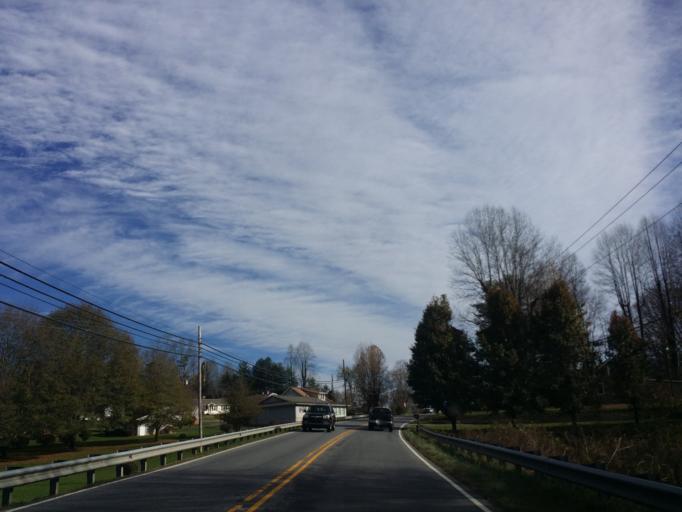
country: US
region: North Carolina
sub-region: McDowell County
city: West Marion
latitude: 35.6875
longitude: -82.0796
